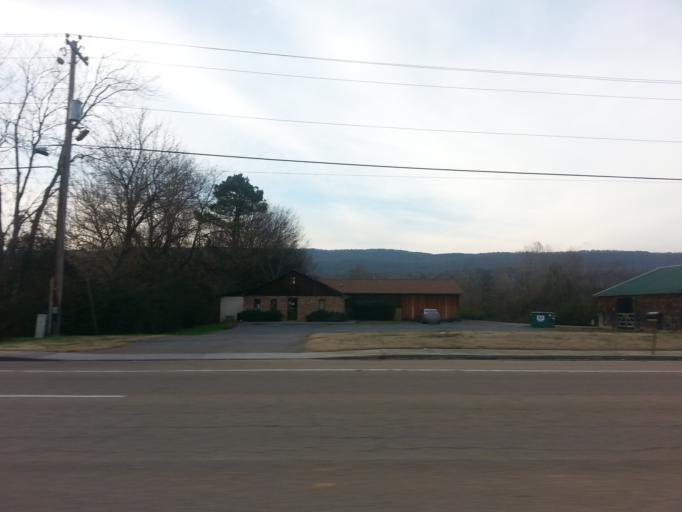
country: US
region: Tennessee
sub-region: Rhea County
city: Dayton
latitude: 35.5366
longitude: -84.9754
